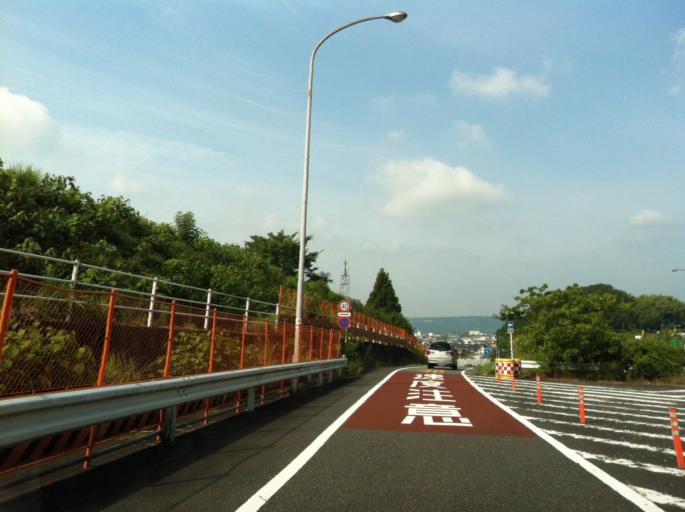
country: JP
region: Shizuoka
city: Shimada
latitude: 34.8464
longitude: 138.1695
